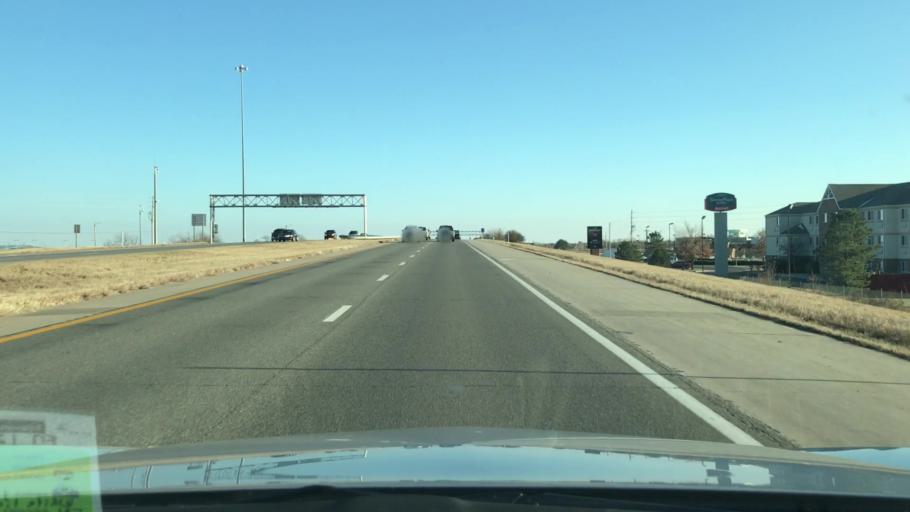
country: US
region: Kansas
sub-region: Sedgwick County
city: Bellaire
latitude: 37.7394
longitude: -97.2286
